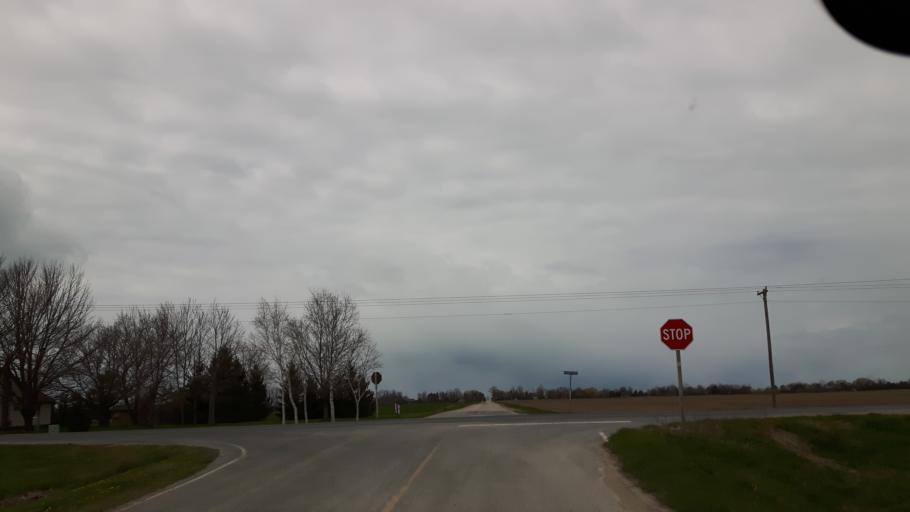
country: CA
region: Ontario
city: Bluewater
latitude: 43.4731
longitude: -81.6984
